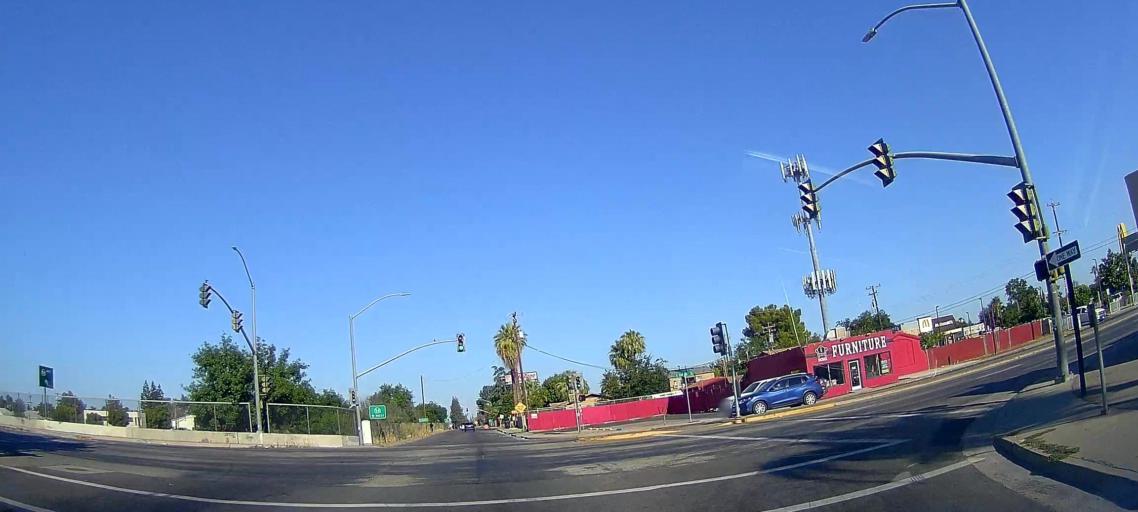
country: US
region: California
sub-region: Kern County
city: Bakersfield
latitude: 35.3530
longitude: -119.0189
